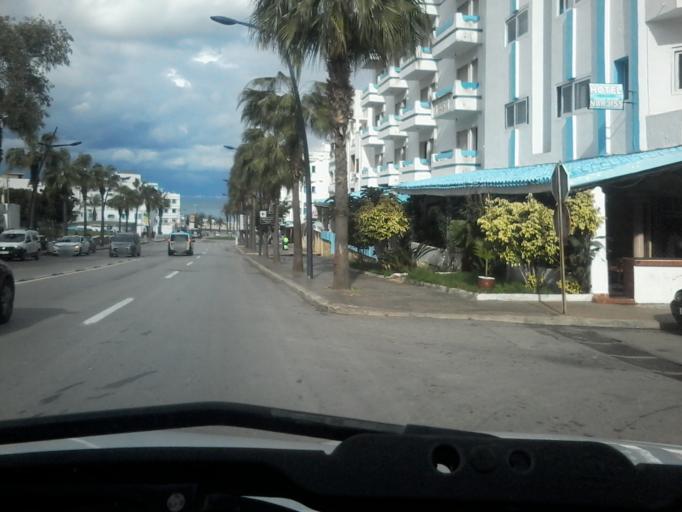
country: MA
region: Tanger-Tetouan
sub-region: Tetouan
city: Martil
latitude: 35.6805
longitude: -5.3211
